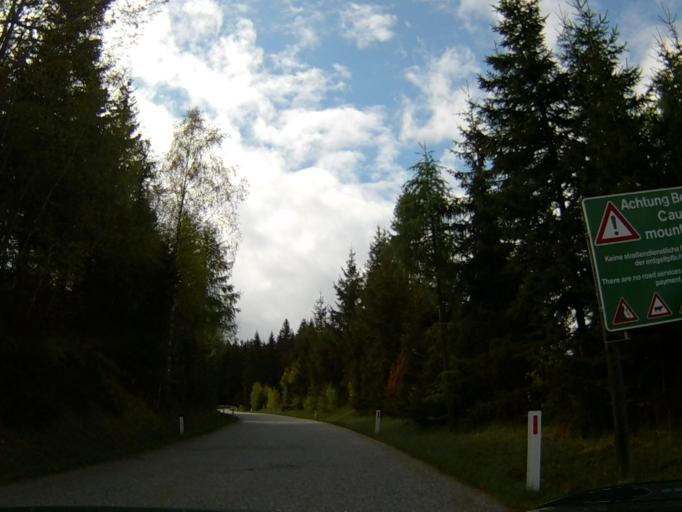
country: AT
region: Carinthia
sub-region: Politischer Bezirk Villach Land
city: Stockenboi
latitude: 46.7395
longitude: 13.5508
